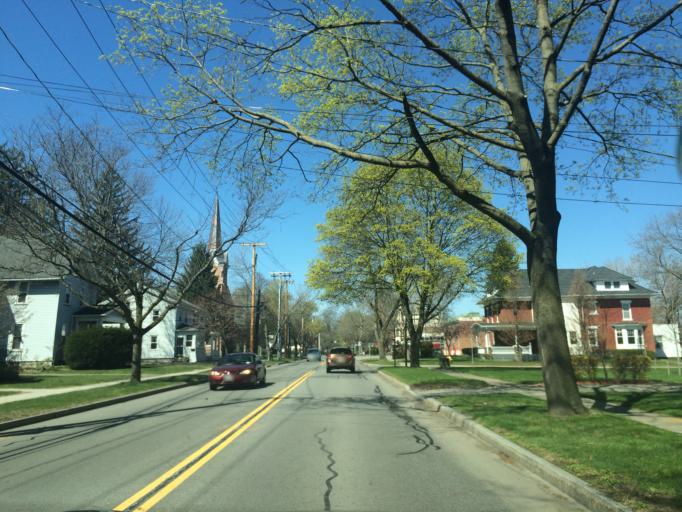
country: US
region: New York
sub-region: Monroe County
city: Fairport
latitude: 43.0985
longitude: -77.4389
